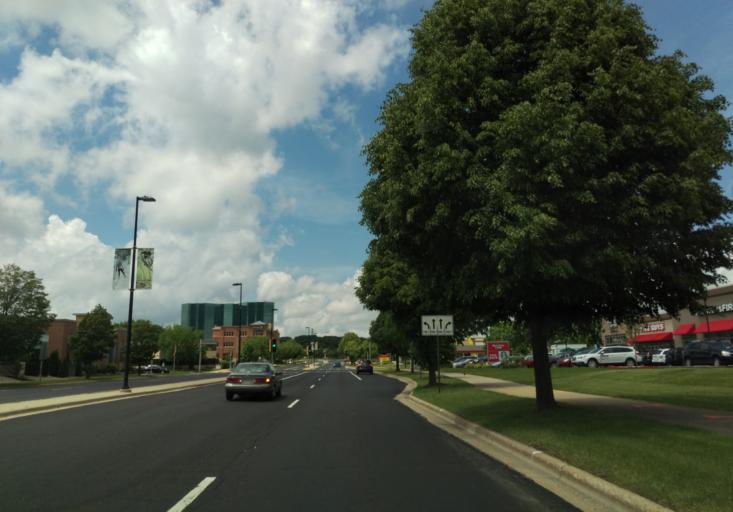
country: US
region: Wisconsin
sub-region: Dane County
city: Middleton
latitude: 43.0902
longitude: -89.5232
